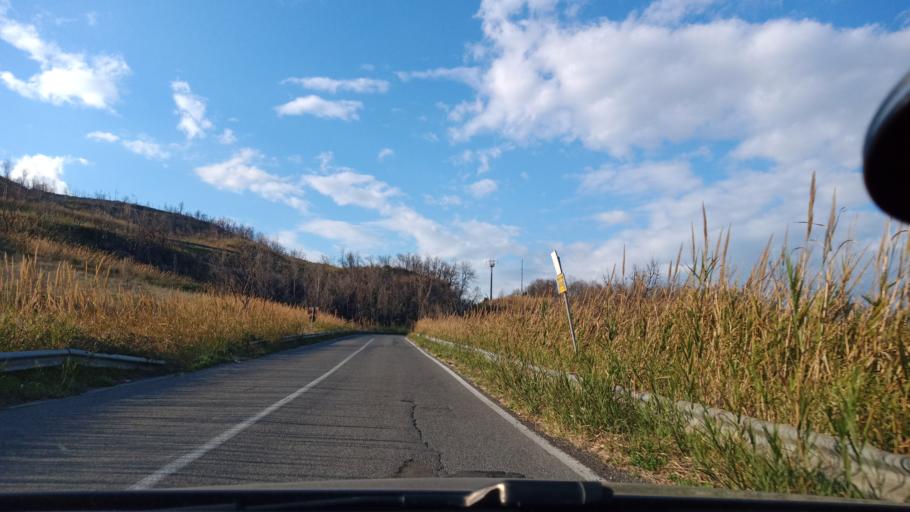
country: IT
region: Latium
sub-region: Citta metropolitana di Roma Capitale
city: Nazzano
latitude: 42.2038
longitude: 12.6049
